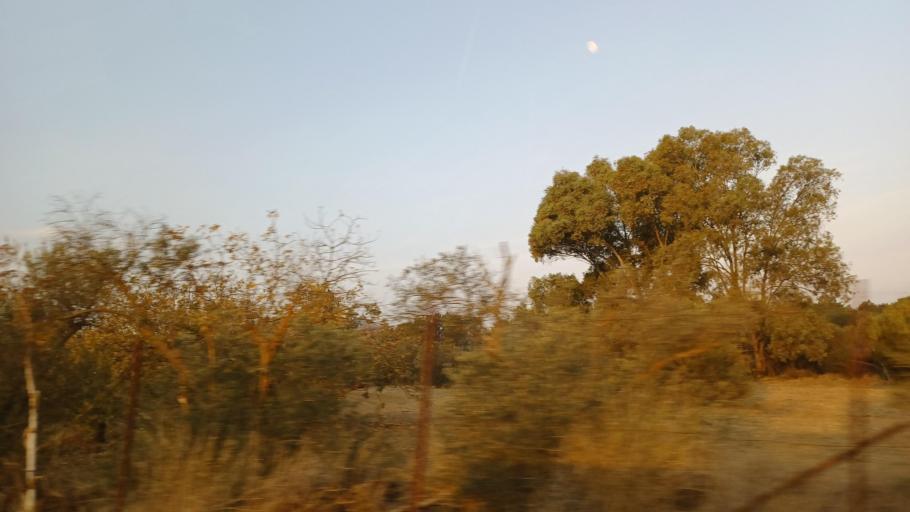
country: CY
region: Larnaka
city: Mosfiloti
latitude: 34.9412
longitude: 33.4130
